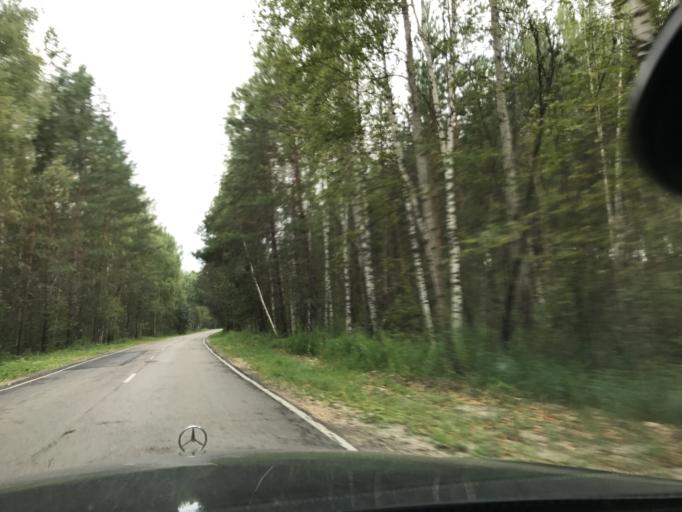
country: RU
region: Nizjnij Novgorod
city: Taremskoye
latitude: 55.9981
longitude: 42.8776
